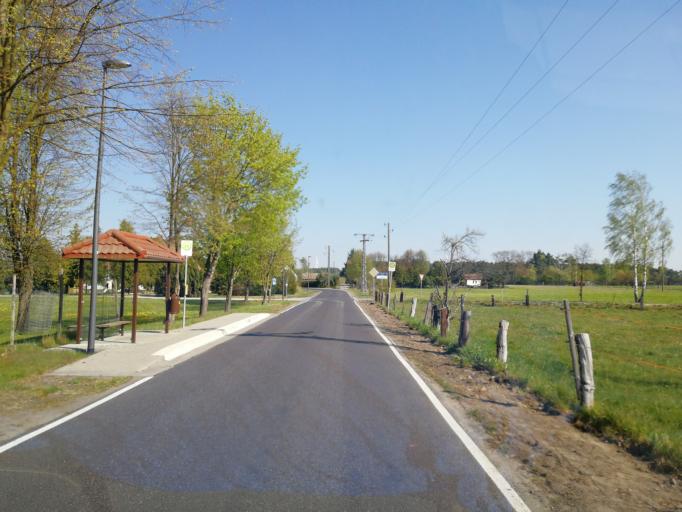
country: DE
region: Brandenburg
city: Bronkow
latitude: 51.7033
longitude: 13.8766
